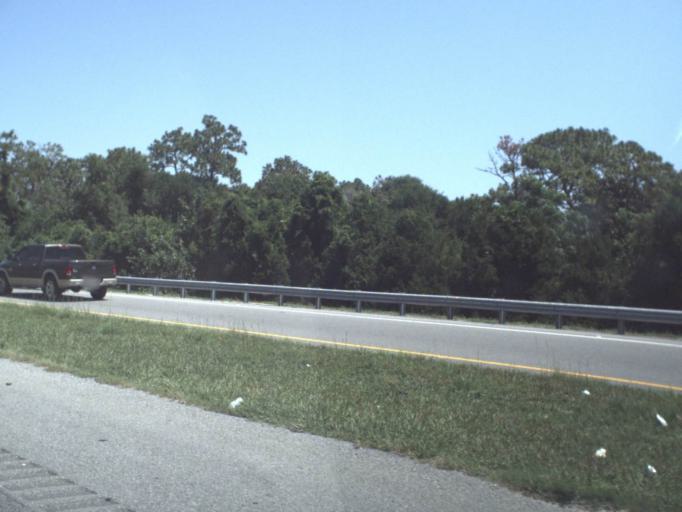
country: US
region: Florida
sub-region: Duval County
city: Jacksonville
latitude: 30.3273
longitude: -81.5286
